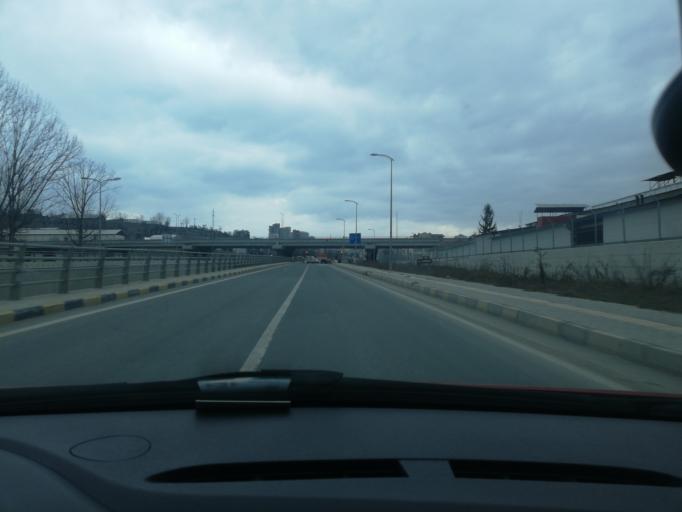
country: TR
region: Kastamonu
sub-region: Cide
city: Kastamonu
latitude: 41.4152
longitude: 33.7991
